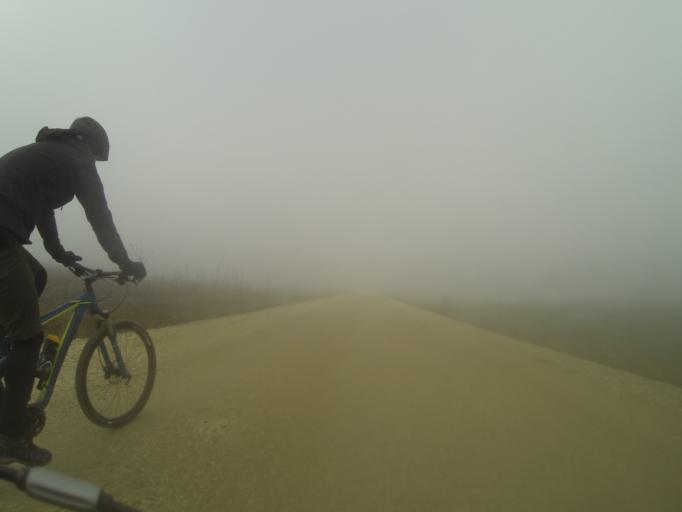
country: RO
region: Mehedinti
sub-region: Comuna Baclesu
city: Baclesu
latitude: 44.4513
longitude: 23.1242
